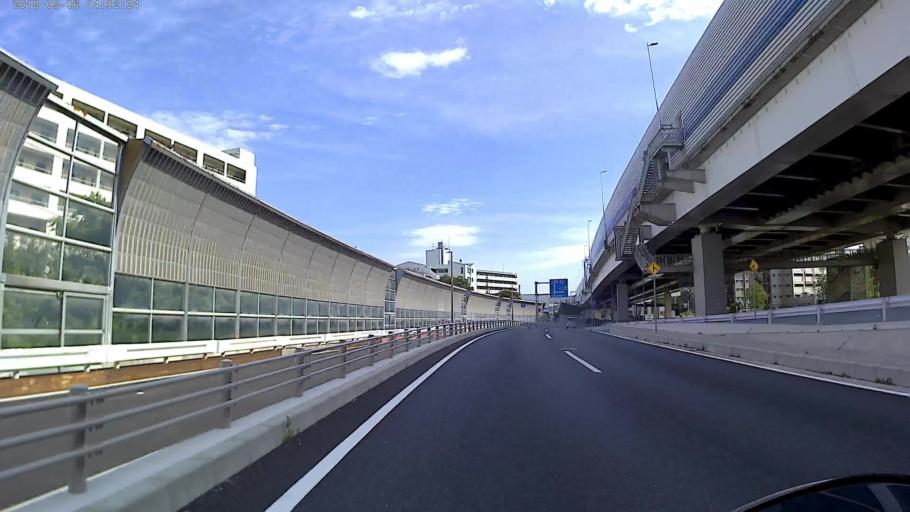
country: JP
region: Kanagawa
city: Yokohama
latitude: 35.4286
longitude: 139.6716
